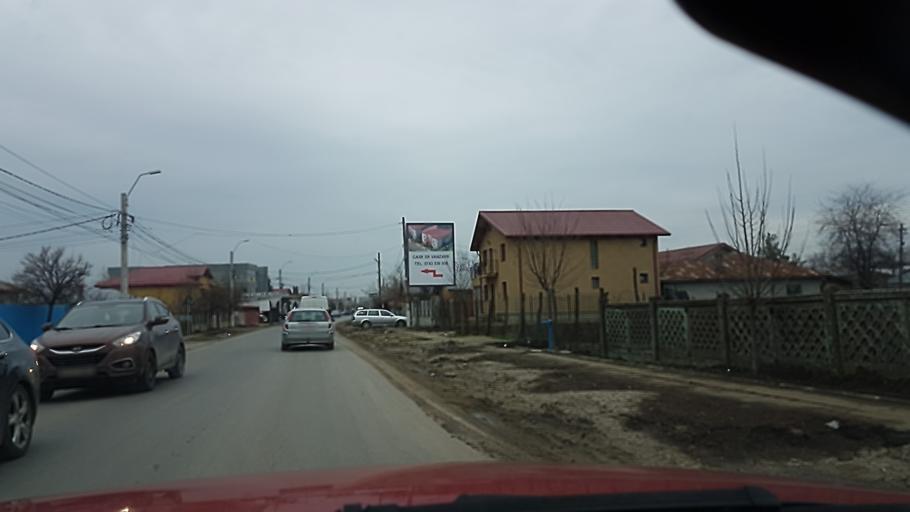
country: RO
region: Ilfov
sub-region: Comuna Tunari
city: Tunari
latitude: 44.5446
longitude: 26.1421
